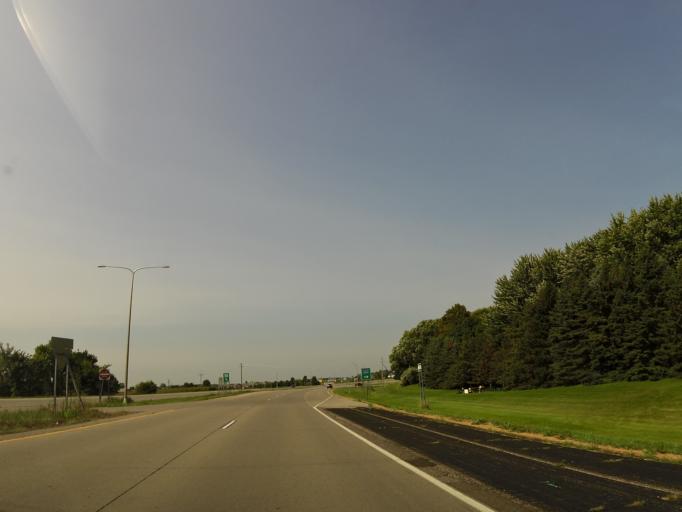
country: US
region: Minnesota
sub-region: Carver County
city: Cologne
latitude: 44.7660
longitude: -93.7774
